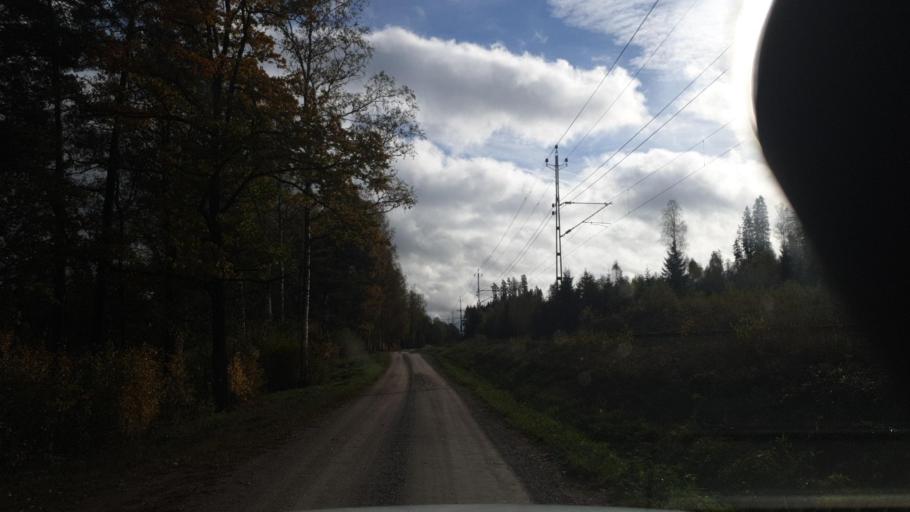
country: SE
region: Vaermland
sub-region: Karlstads Kommun
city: Edsvalla
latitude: 59.6153
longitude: 12.9676
